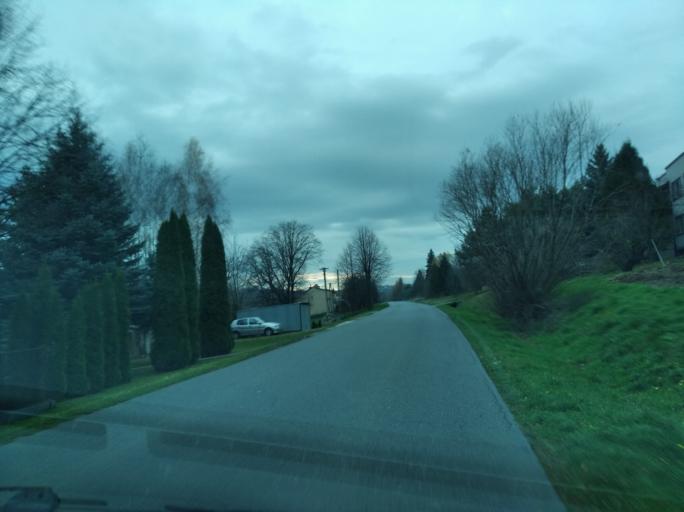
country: PL
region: Subcarpathian Voivodeship
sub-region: Powiat ropczycko-sedziszowski
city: Iwierzyce
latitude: 49.9989
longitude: 21.7448
